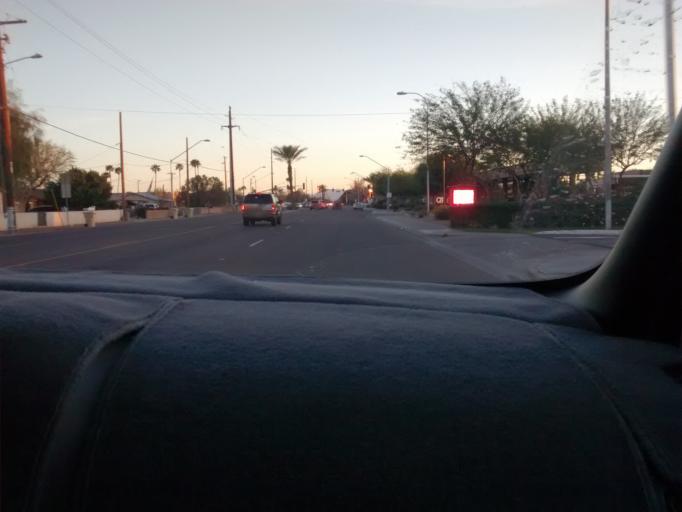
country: US
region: Arizona
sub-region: Maricopa County
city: Glendale
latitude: 33.5403
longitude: -112.2032
